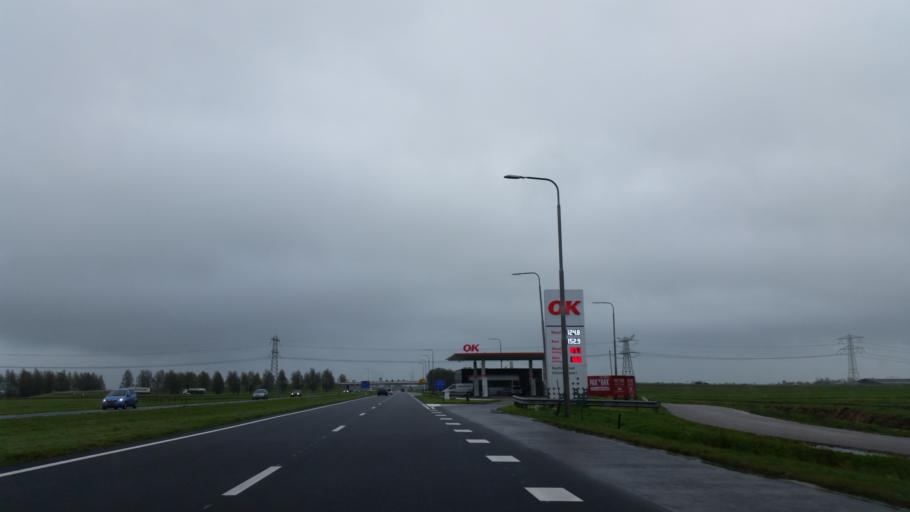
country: NL
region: Friesland
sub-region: Gemeente Leeuwarden
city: Goutum
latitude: 53.1720
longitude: 5.8265
